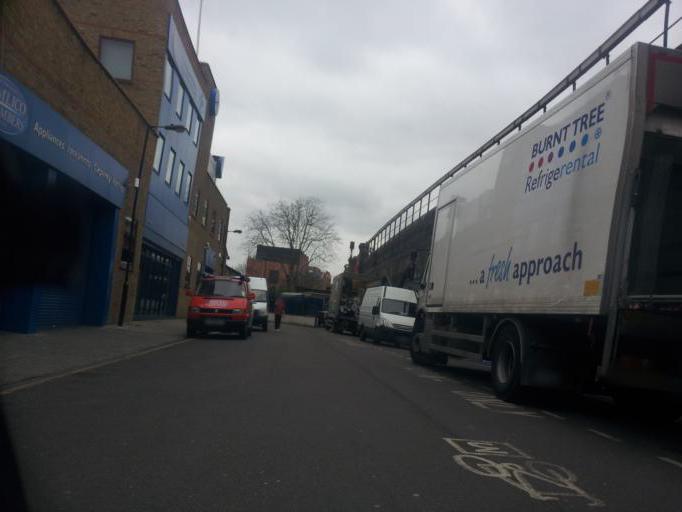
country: GB
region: England
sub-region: Greater London
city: Lambeth
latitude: 51.4950
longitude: -0.1159
